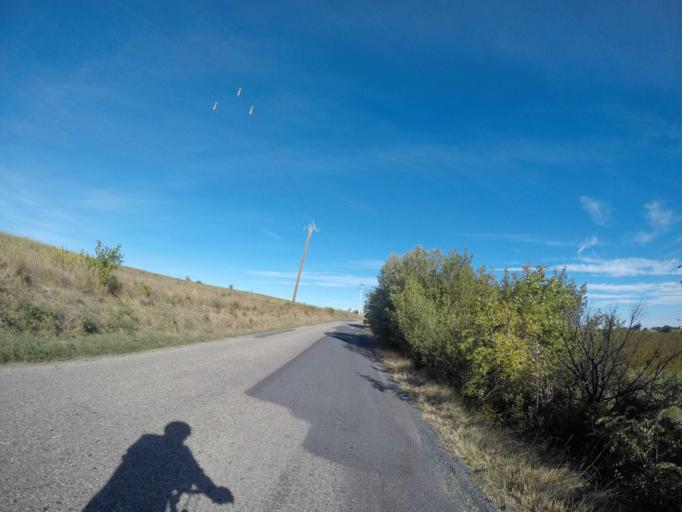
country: FR
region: Languedoc-Roussillon
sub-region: Departement des Pyrenees-Orientales
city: Trouillas
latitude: 42.5979
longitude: 2.8077
